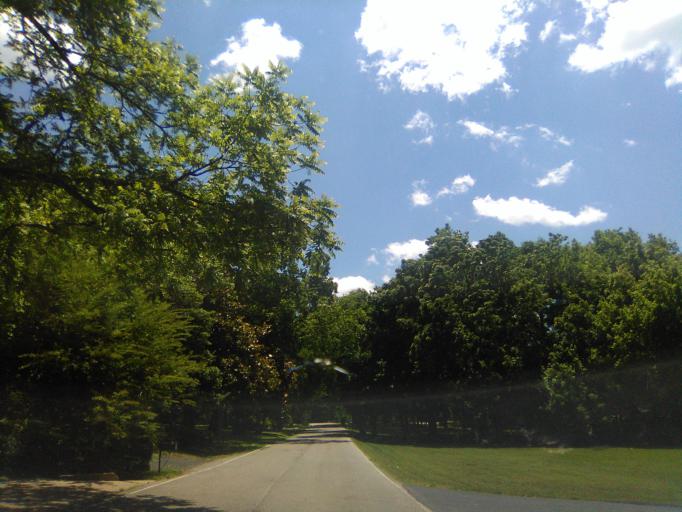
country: US
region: Tennessee
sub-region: Davidson County
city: Belle Meade
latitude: 36.1098
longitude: -86.8527
